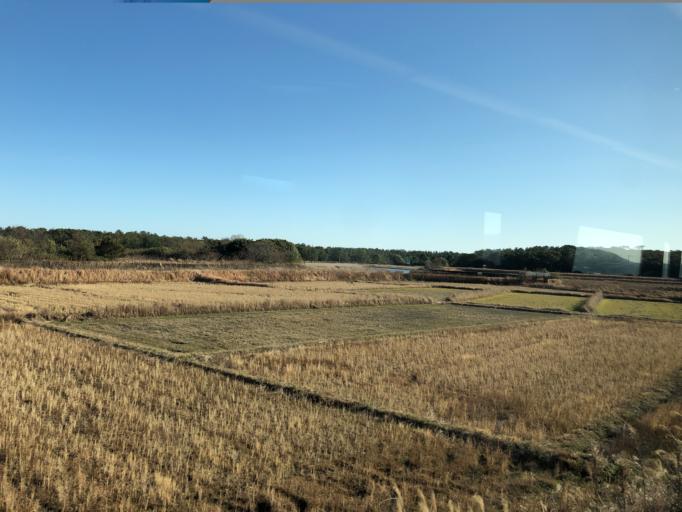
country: JP
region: Kochi
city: Nakamura
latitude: 33.0339
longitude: 133.0188
